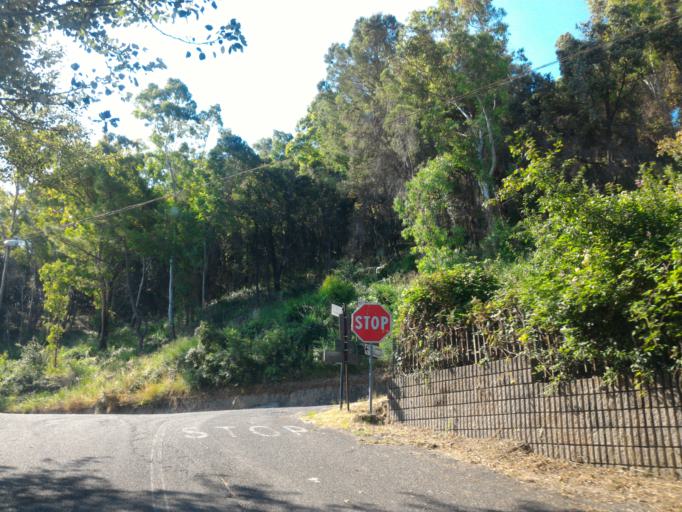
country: IT
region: Calabria
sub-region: Provincia di Crotone
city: Ciro
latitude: 39.3813
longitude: 17.0679
